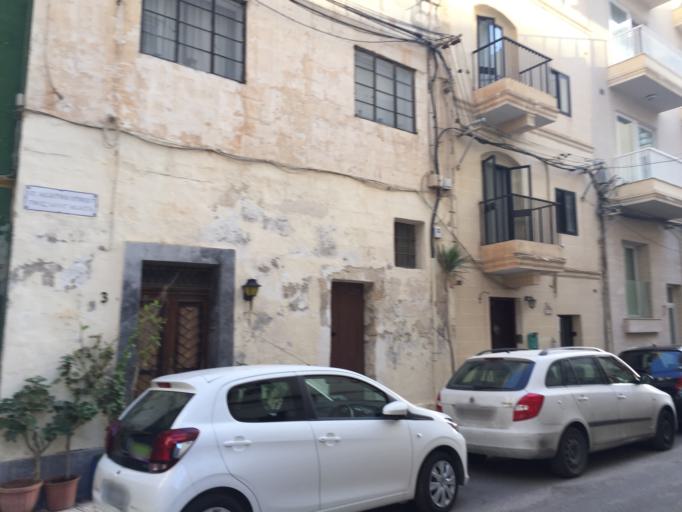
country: MT
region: Tas-Sliema
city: Sliema
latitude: 35.9088
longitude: 14.5011
